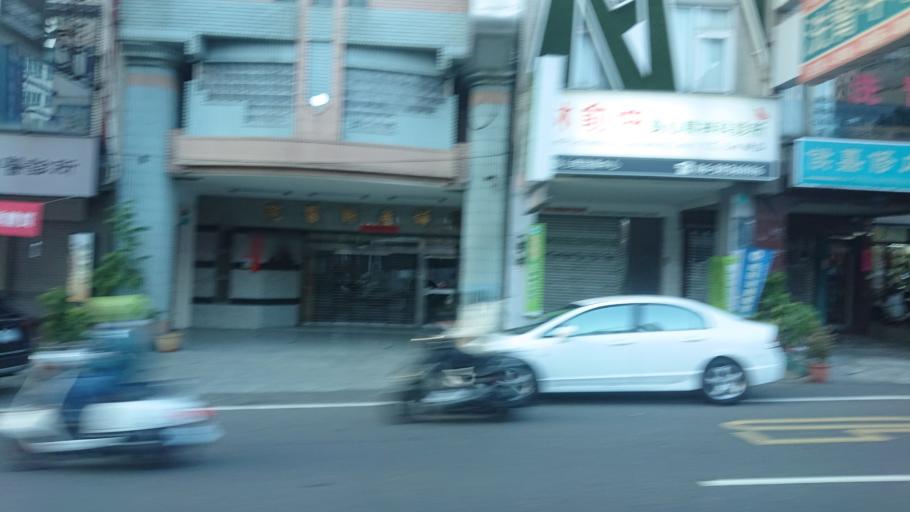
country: TW
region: Taiwan
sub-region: Tainan
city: Tainan
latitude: 23.0119
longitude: 120.2268
